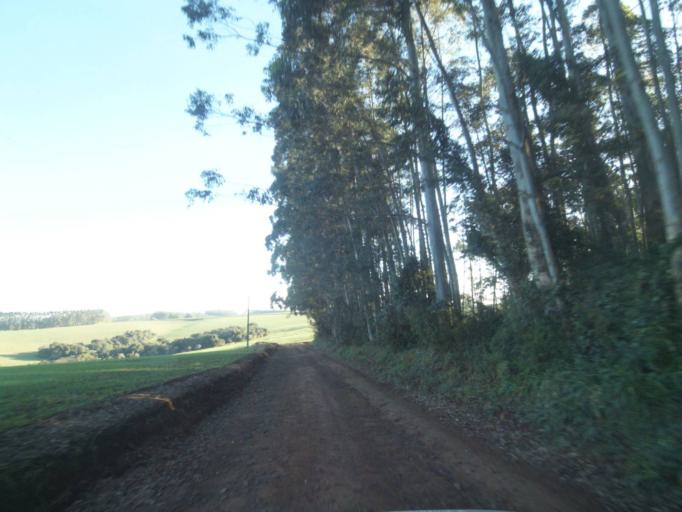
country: BR
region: Parana
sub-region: Telemaco Borba
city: Telemaco Borba
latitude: -24.4790
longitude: -50.5893
